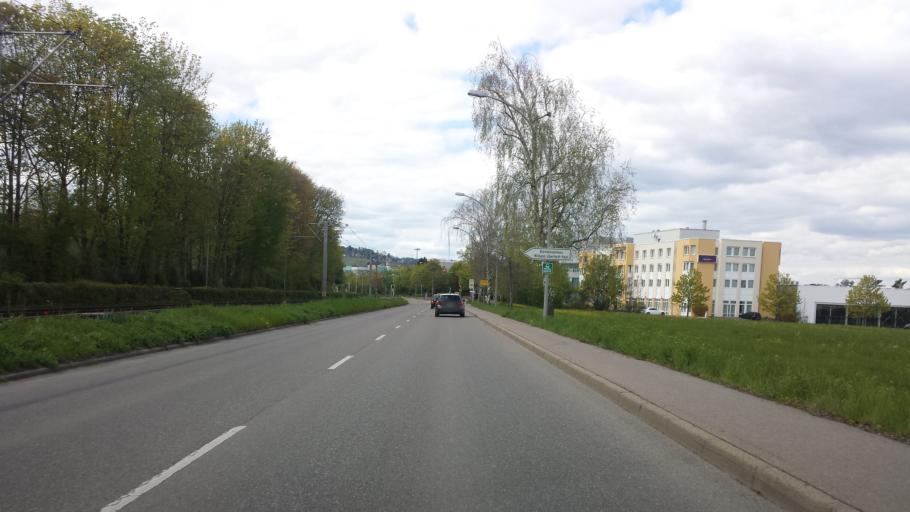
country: DE
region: Baden-Wuerttemberg
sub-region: Regierungsbezirk Stuttgart
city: Gerlingen
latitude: 48.8024
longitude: 9.0788
